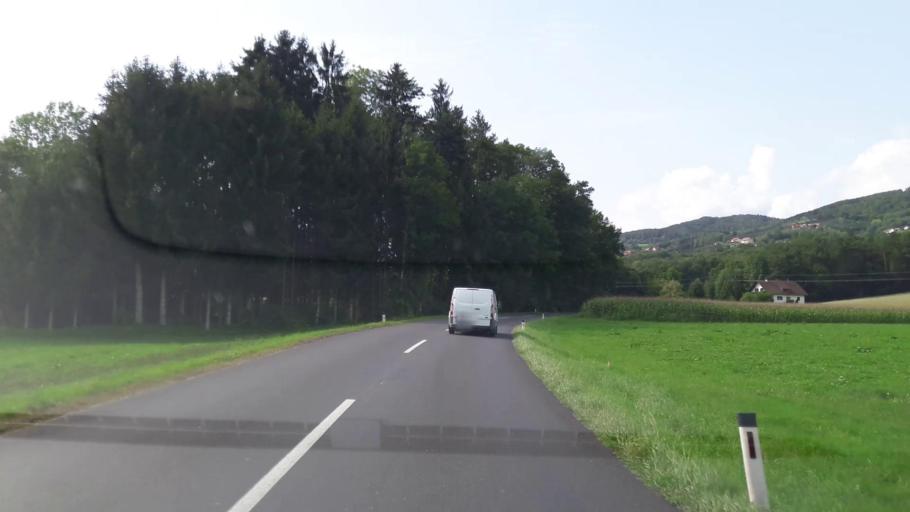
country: AT
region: Styria
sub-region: Politischer Bezirk Hartberg-Fuerstenfeld
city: Kaibing
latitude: 47.2321
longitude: 15.8415
